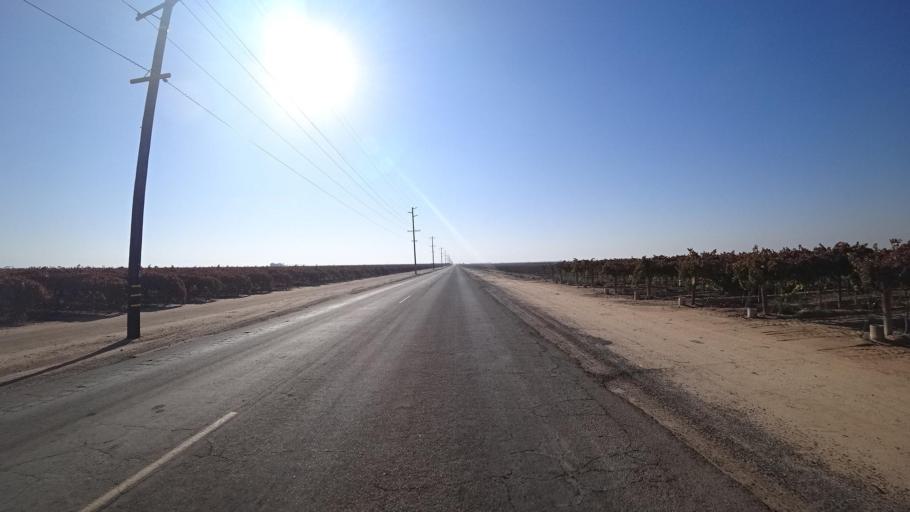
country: US
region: California
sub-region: Kern County
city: Delano
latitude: 35.7390
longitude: -119.2052
